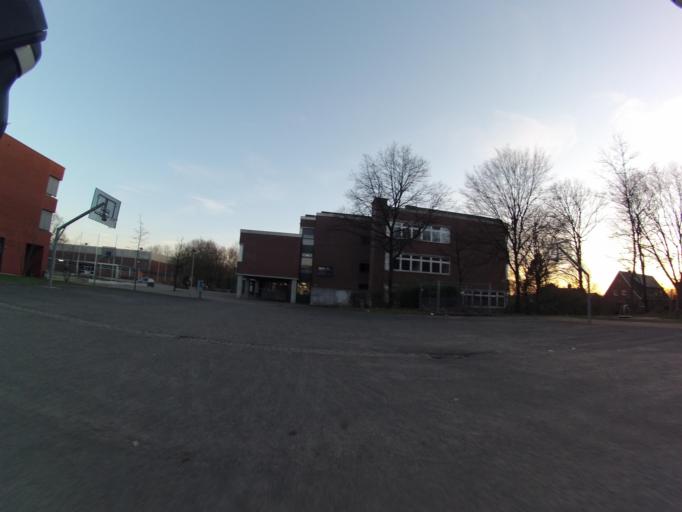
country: DE
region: North Rhine-Westphalia
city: Ibbenburen
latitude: 52.2691
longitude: 7.7348
